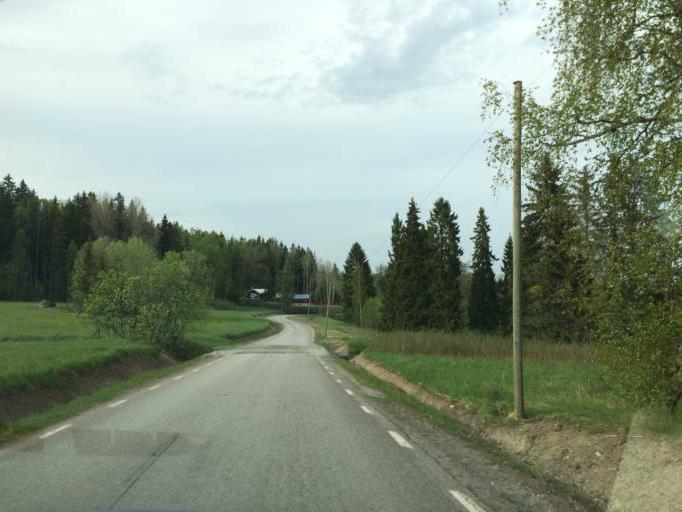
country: SE
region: Vaestmanland
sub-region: Kopings Kommun
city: Koping
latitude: 59.5862
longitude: 15.9866
